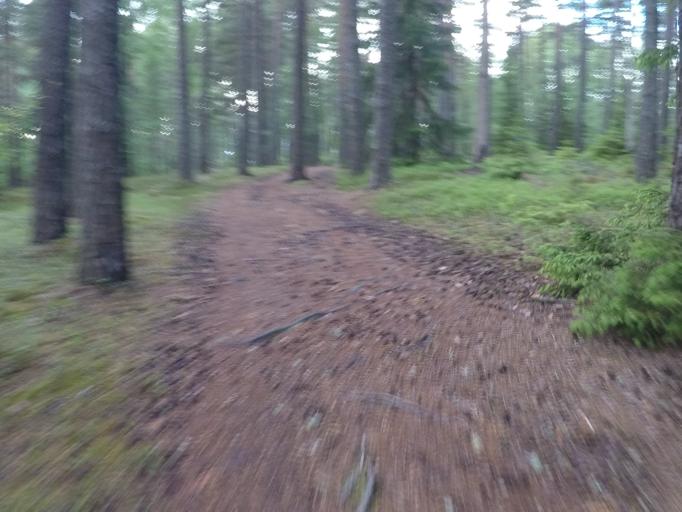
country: SE
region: Soedermanland
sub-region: Eskilstuna Kommun
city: Hallbybrunn
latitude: 59.4008
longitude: 16.3992
